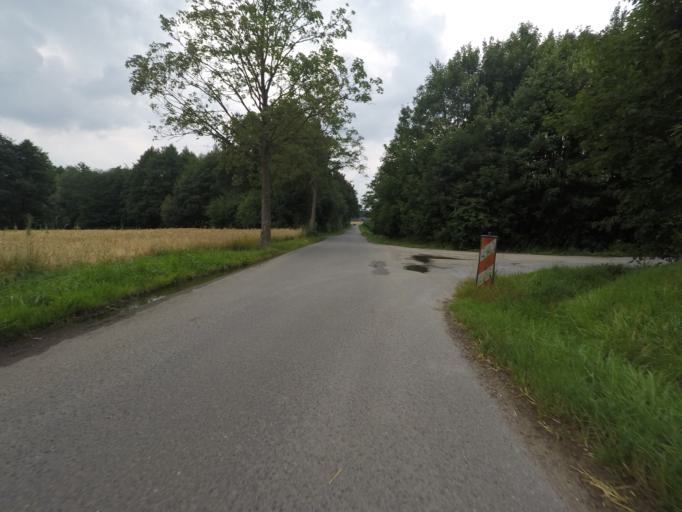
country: DE
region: North Rhine-Westphalia
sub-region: Regierungsbezirk Detmold
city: Hiddenhausen
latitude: 52.1186
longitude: 8.6217
